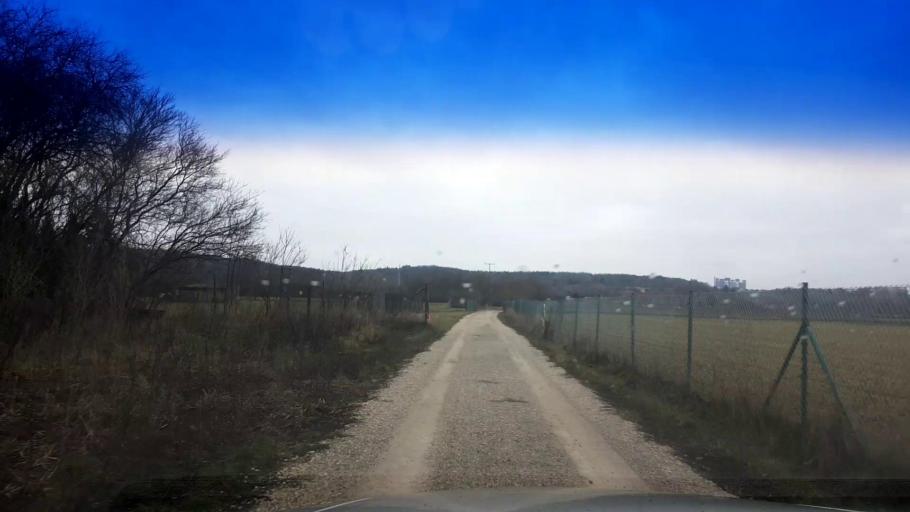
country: DE
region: Bavaria
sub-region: Upper Franconia
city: Bamberg
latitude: 49.8735
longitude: 10.9267
